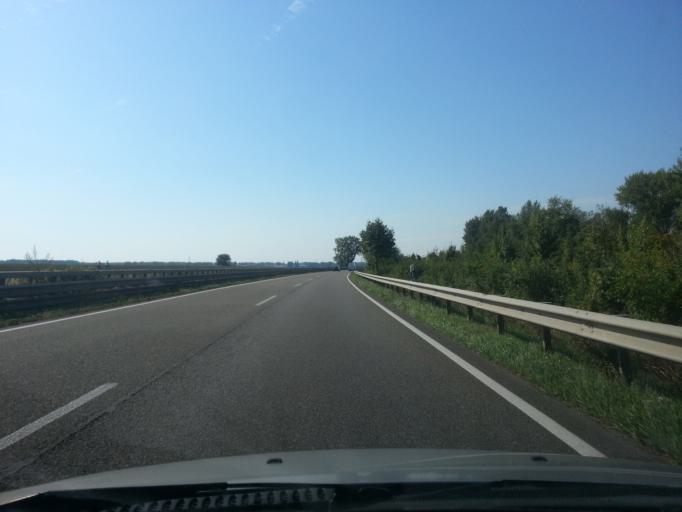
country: DE
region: Rheinland-Pfalz
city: Bobenheim-Roxheim
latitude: 49.5896
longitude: 8.4047
